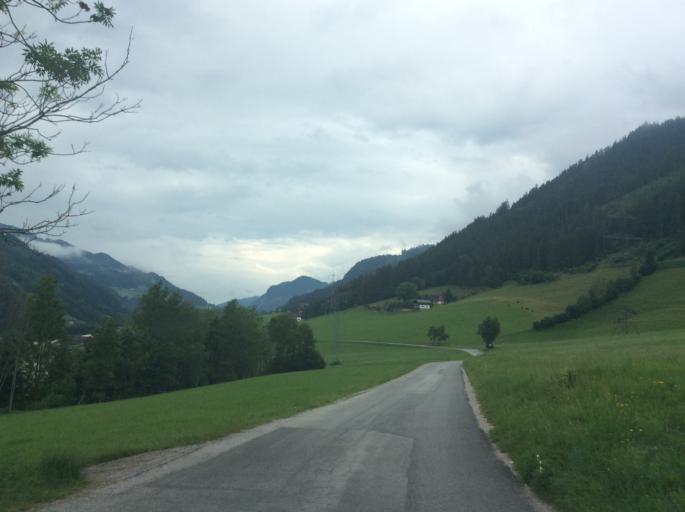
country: AT
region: Styria
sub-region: Politischer Bezirk Liezen
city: Schladming
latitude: 47.3922
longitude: 13.6640
